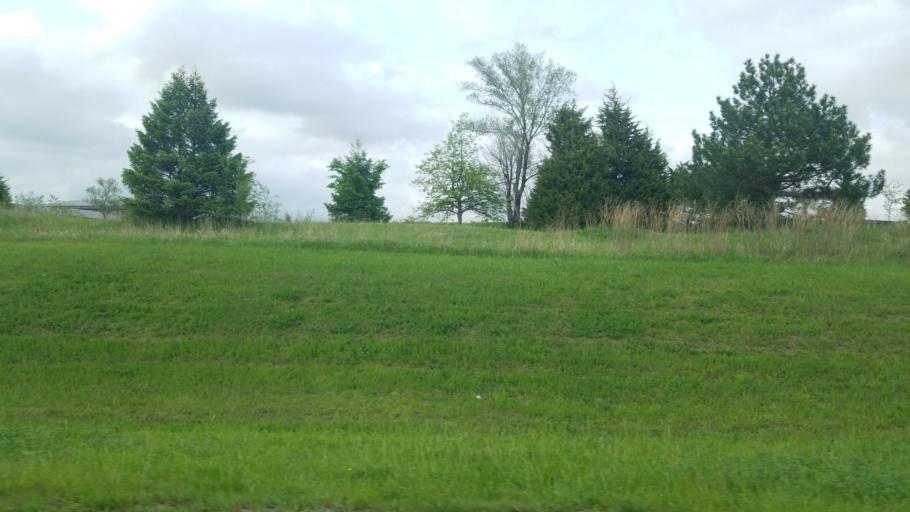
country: US
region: Nebraska
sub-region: Lancaster County
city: Lincoln
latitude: 40.8724
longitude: -96.7225
